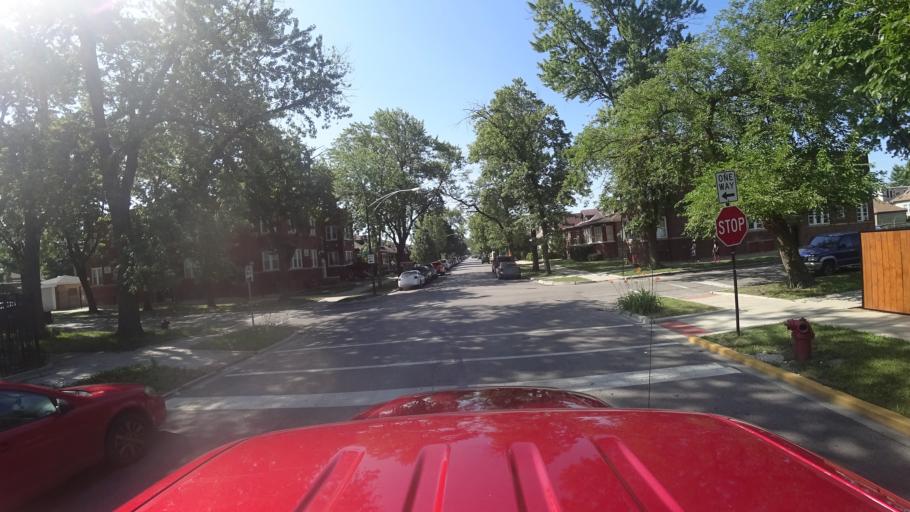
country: US
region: Illinois
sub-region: Cook County
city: Hometown
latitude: 41.7885
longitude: -87.6888
